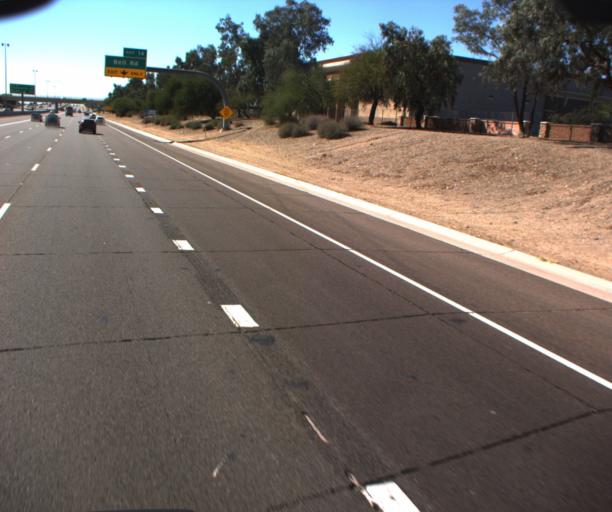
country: US
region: Arizona
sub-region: Maricopa County
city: Sun City
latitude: 33.6474
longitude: -112.2338
